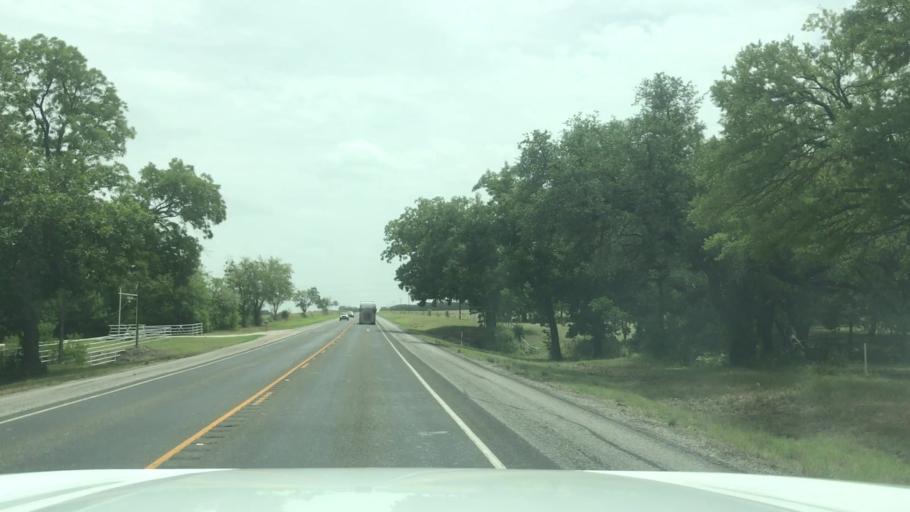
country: US
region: Texas
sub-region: Bosque County
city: Meridian
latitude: 31.8786
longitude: -97.6424
